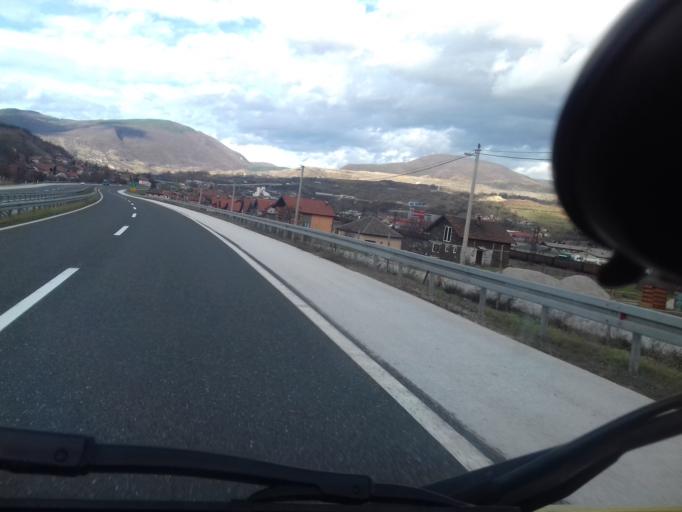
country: BA
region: Federation of Bosnia and Herzegovina
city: Kakanj
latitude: 44.1164
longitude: 18.1090
